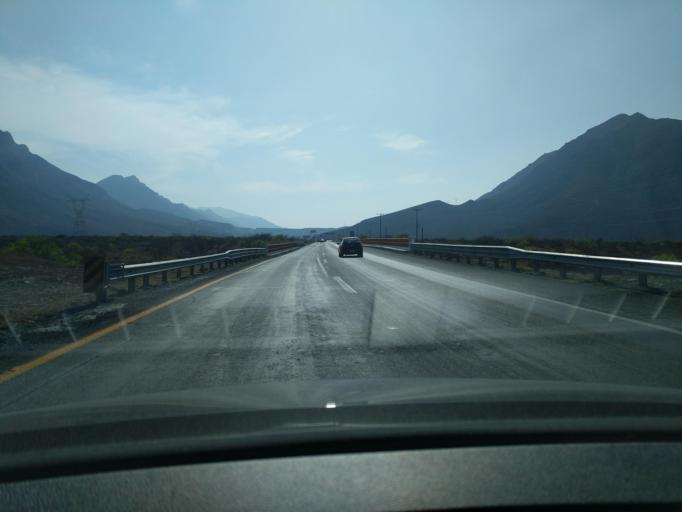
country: MX
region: Nuevo Leon
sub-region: Garcia
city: Las Torres de Guadalupe
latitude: 25.6629
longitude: -100.7078
